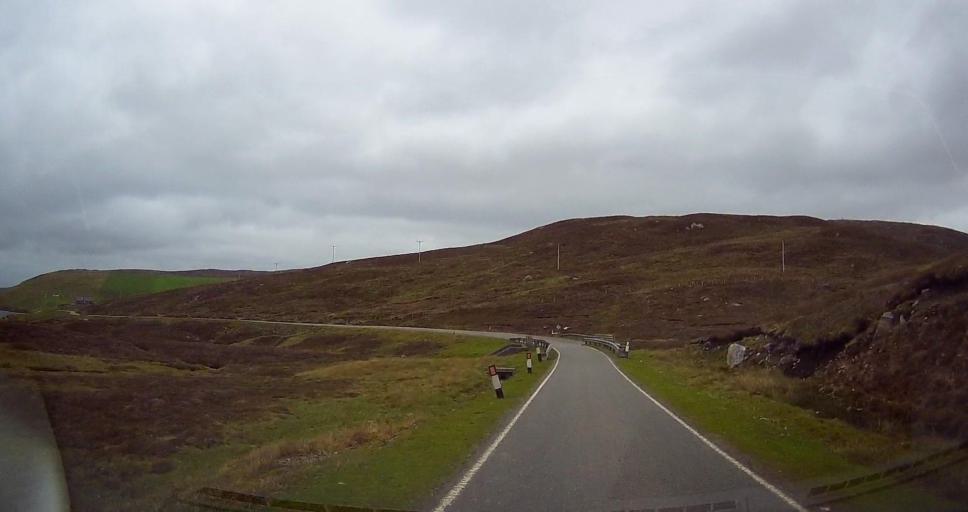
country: GB
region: Scotland
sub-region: Shetland Islands
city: Lerwick
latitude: 60.3296
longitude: -1.3368
